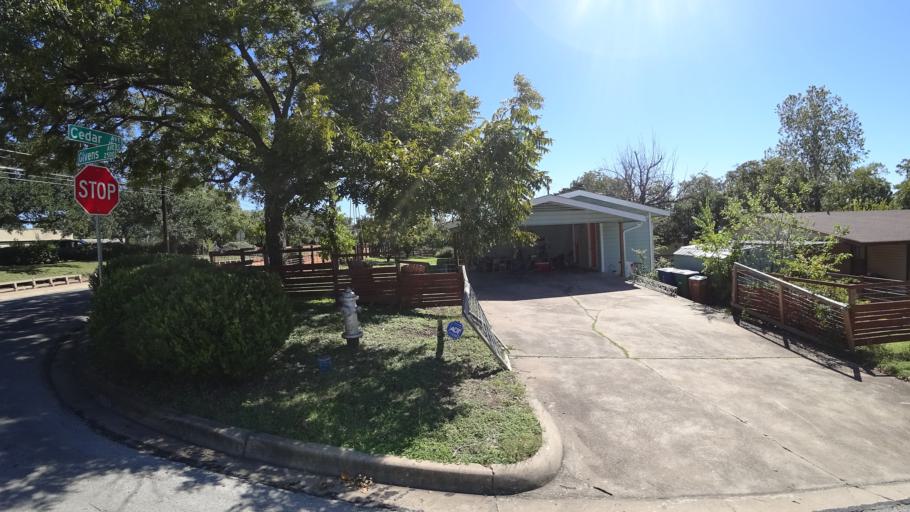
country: US
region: Texas
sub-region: Travis County
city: Austin
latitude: 30.2817
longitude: -97.7148
